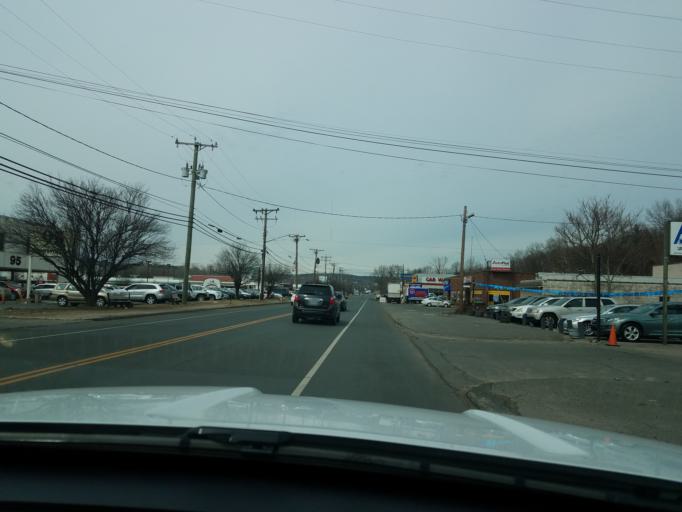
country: US
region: Connecticut
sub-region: New Haven County
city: Waterbury
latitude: 41.5594
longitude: -73.0527
